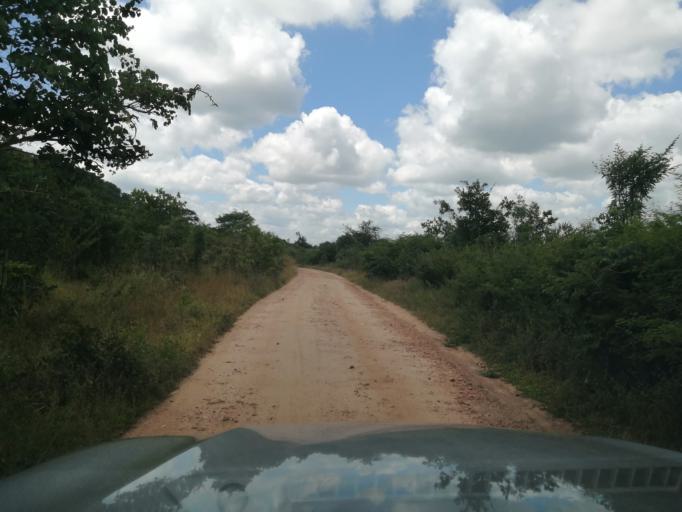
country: ZM
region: Lusaka
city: Lusaka
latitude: -15.1392
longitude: 27.9230
